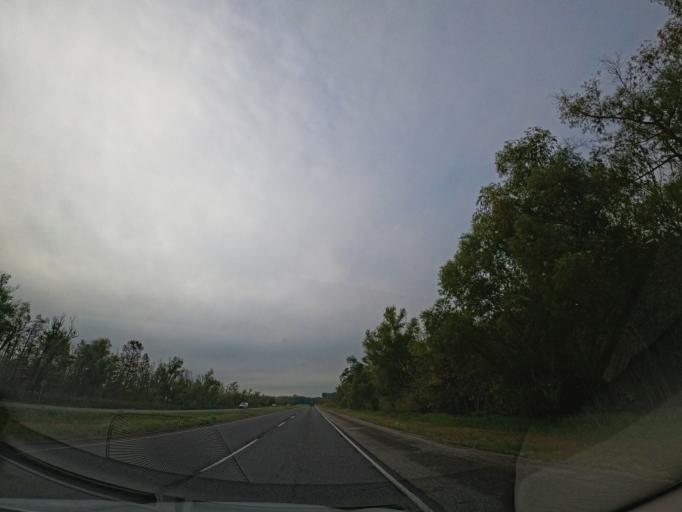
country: US
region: Louisiana
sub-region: Terrebonne Parish
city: Houma
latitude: 29.6296
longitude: -90.6619
